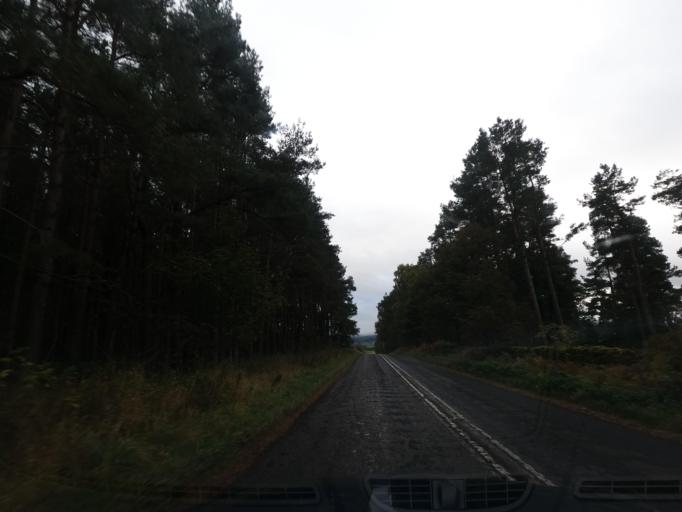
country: GB
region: England
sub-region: Northumberland
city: Doddington
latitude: 55.6019
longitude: -2.0017
